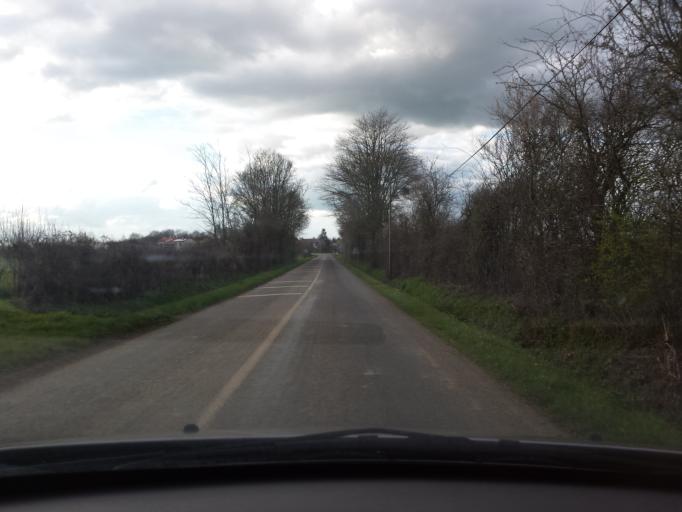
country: FR
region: Pays de la Loire
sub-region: Departement de la Vendee
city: Sainte-Cecile
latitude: 46.7193
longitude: -1.1140
